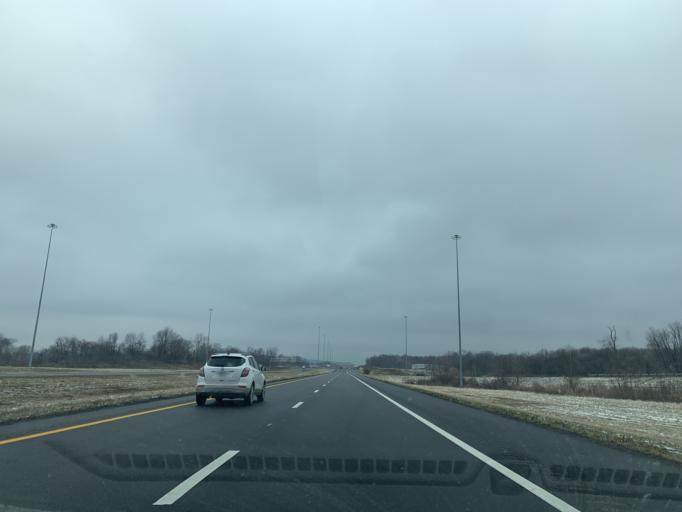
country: US
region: Ohio
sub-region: Licking County
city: Granville South
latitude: 40.0734
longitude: -82.6051
